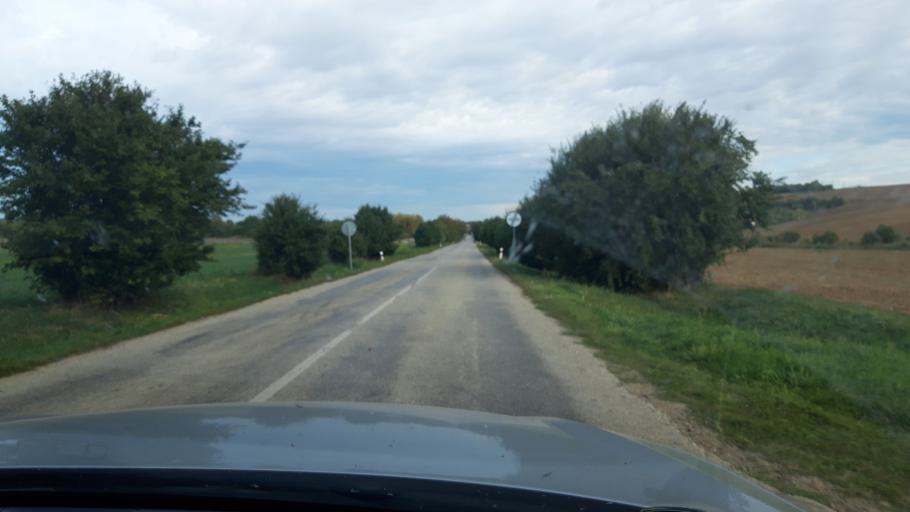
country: SK
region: Nitriansky
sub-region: Okres Nitra
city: Vrable
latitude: 48.1262
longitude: 18.3344
